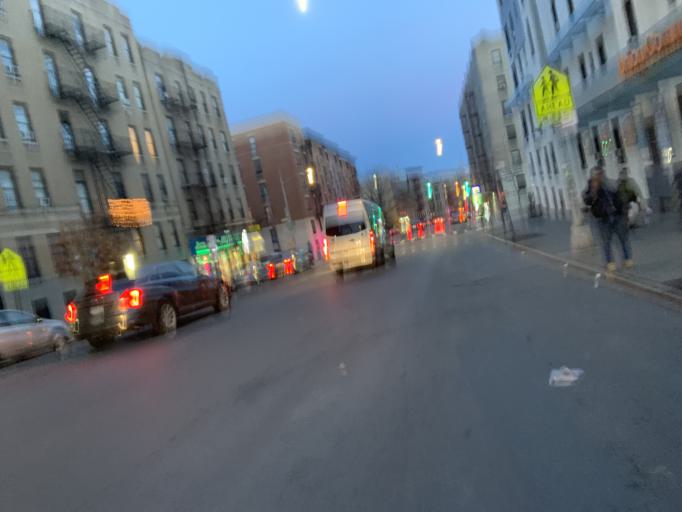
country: US
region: New York
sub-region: New York County
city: Inwood
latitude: 40.8609
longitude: -73.8960
